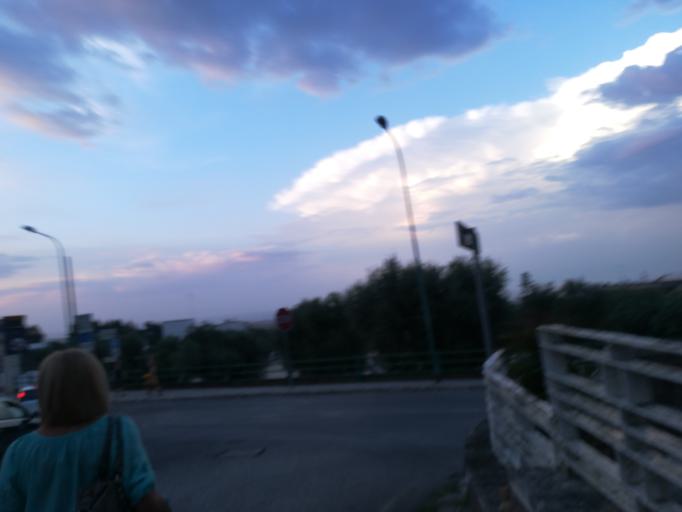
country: IT
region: Apulia
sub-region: Provincia di Brindisi
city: Ostuni
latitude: 40.7315
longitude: 17.5704
